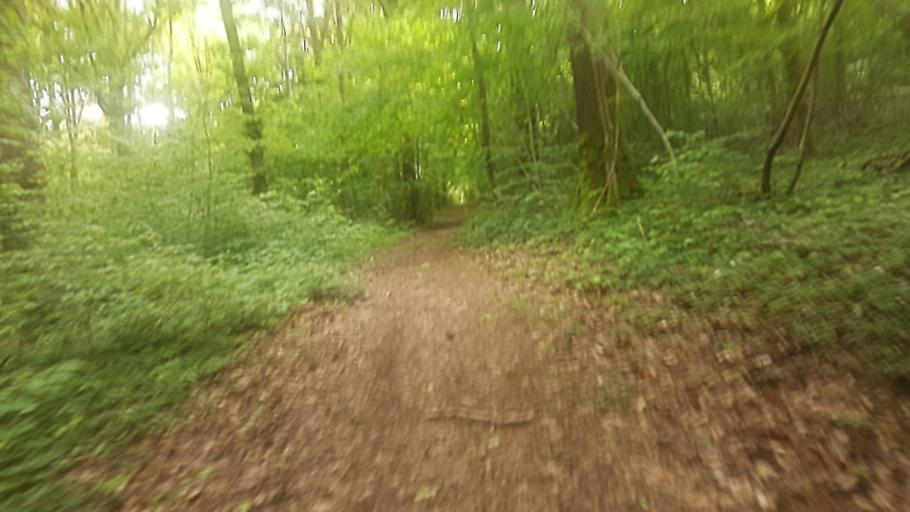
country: FR
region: Champagne-Ardenne
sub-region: Departement des Ardennes
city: Haybes
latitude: 50.0550
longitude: 4.6062
